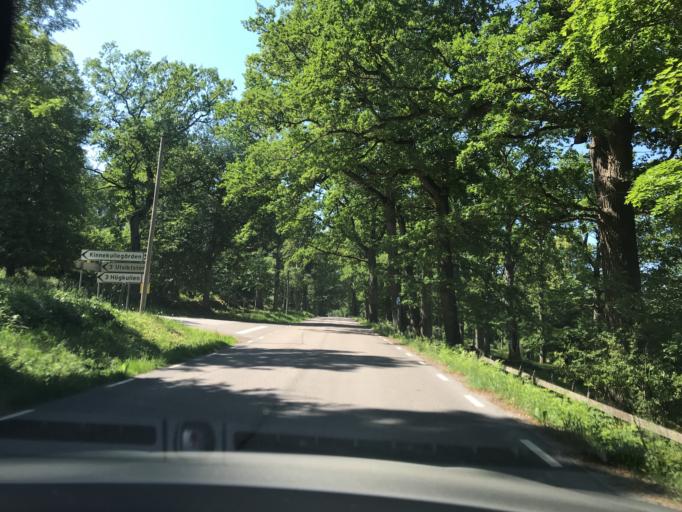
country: SE
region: Vaestra Goetaland
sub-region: Gotene Kommun
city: Goetene
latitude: 58.6220
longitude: 13.4205
